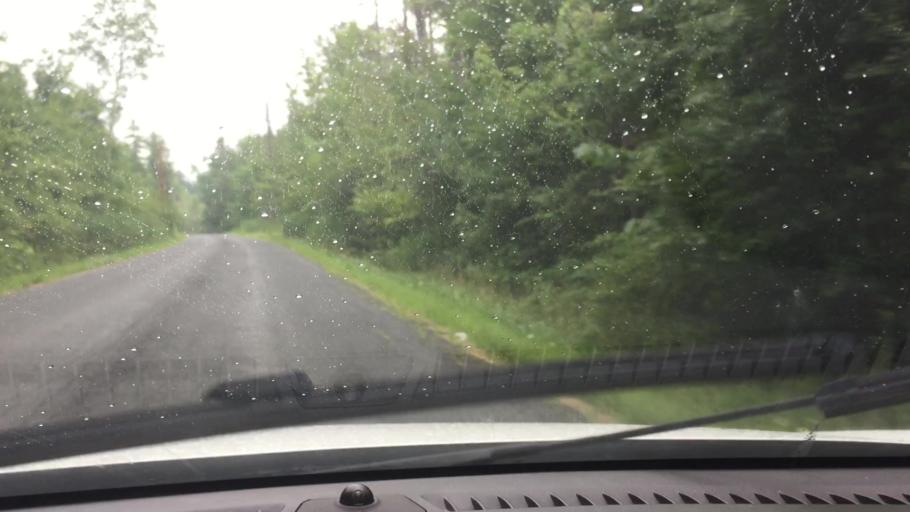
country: US
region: Massachusetts
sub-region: Berkshire County
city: Lee
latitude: 42.3087
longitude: -73.2841
